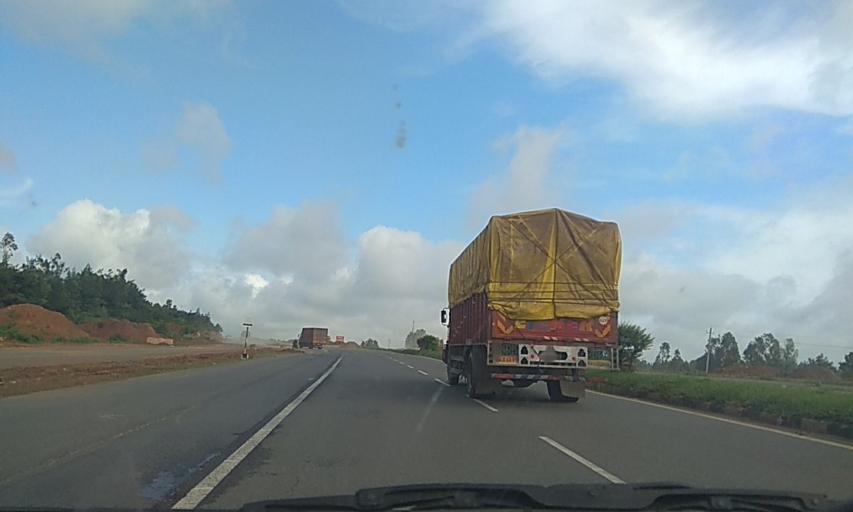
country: IN
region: Karnataka
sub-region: Haveri
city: Shiggaon
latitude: 15.0324
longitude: 75.1793
